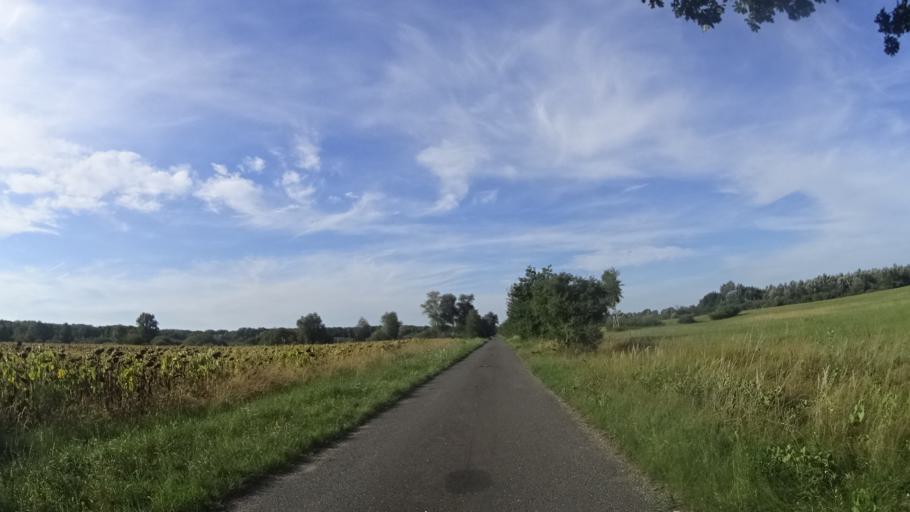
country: AT
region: Lower Austria
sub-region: Politischer Bezirk Ganserndorf
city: Drosing
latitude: 48.5670
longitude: 16.9549
